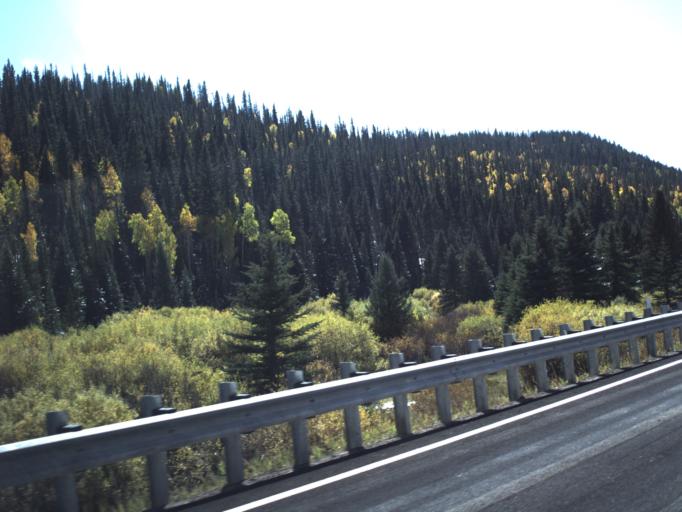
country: US
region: Utah
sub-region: Piute County
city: Junction
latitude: 38.3057
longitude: -112.4182
